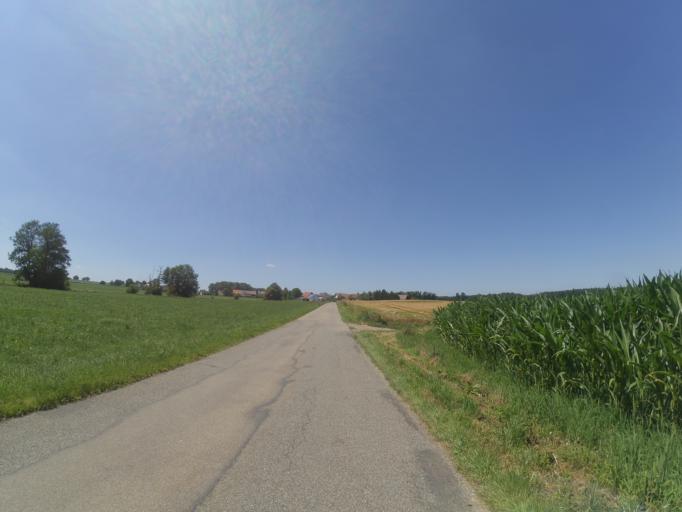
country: DE
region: Baden-Wuerttemberg
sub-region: Tuebingen Region
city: Aulendorf
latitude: 47.9235
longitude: 9.6908
